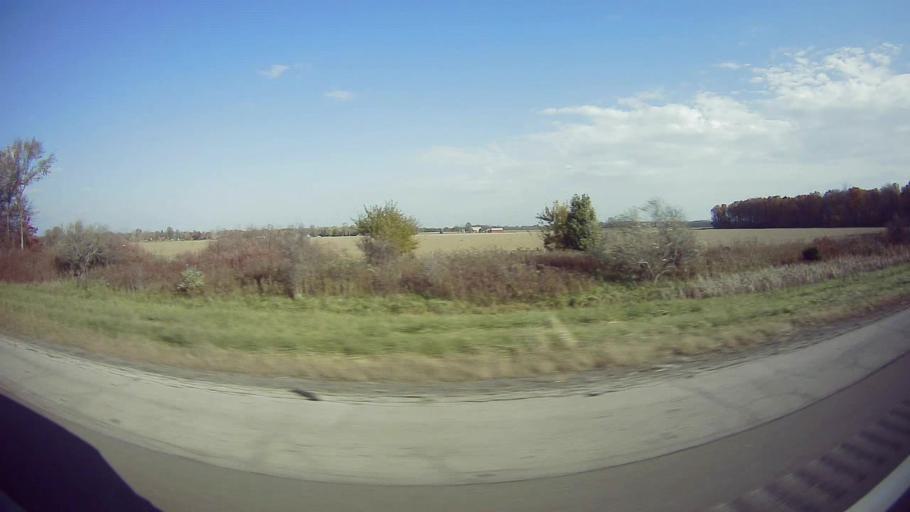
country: US
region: Michigan
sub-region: Monroe County
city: Carleton
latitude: 42.0481
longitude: -83.3537
